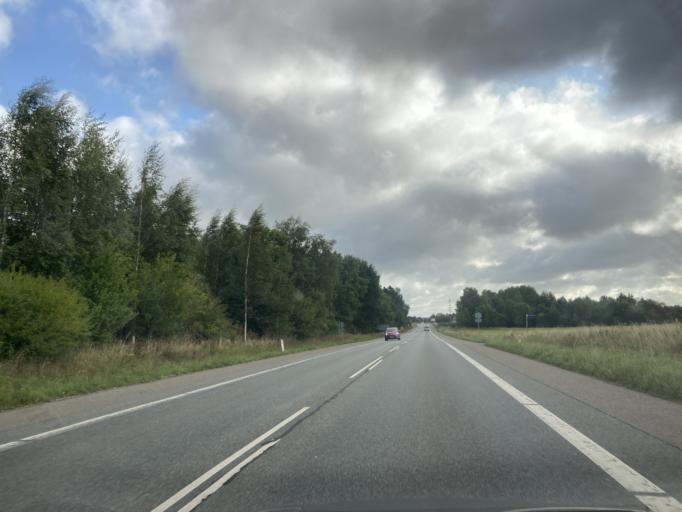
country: DK
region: Capital Region
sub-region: Hillerod Kommune
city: Skaevinge
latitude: 55.9404
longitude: 12.1987
